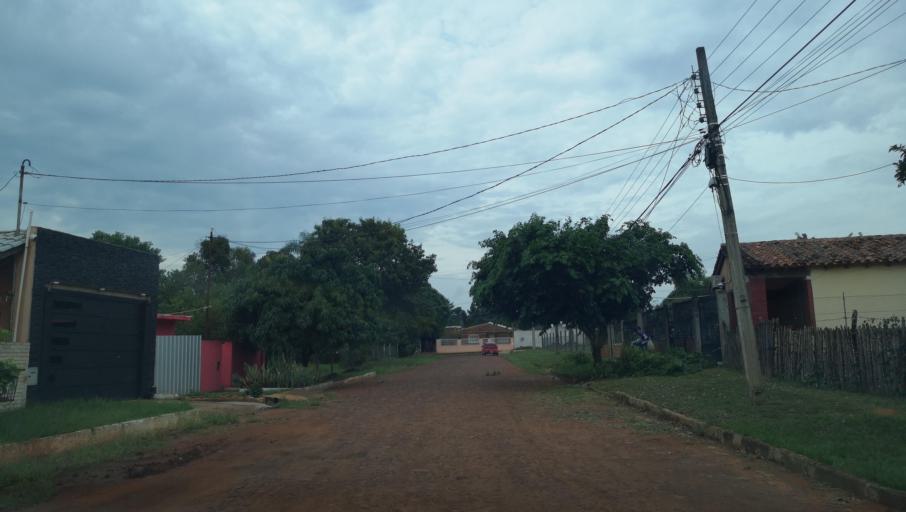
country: PY
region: Misiones
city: Santa Maria
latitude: -26.8820
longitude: -57.0348
